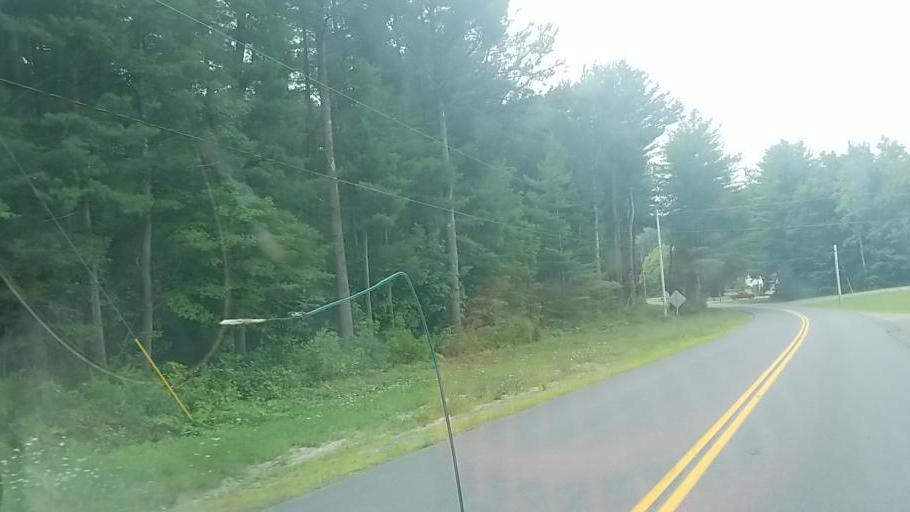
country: US
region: New York
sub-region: Fulton County
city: Johnstown
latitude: 43.0416
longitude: -74.3792
